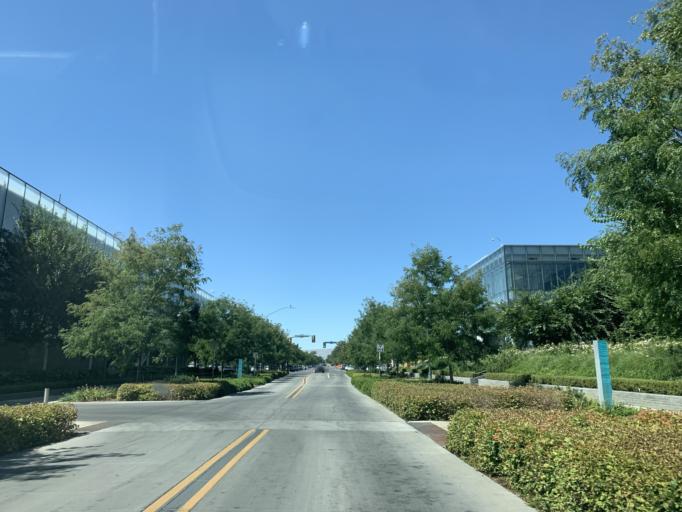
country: US
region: Utah
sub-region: Utah County
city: Provo
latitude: 40.2324
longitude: -111.6609
